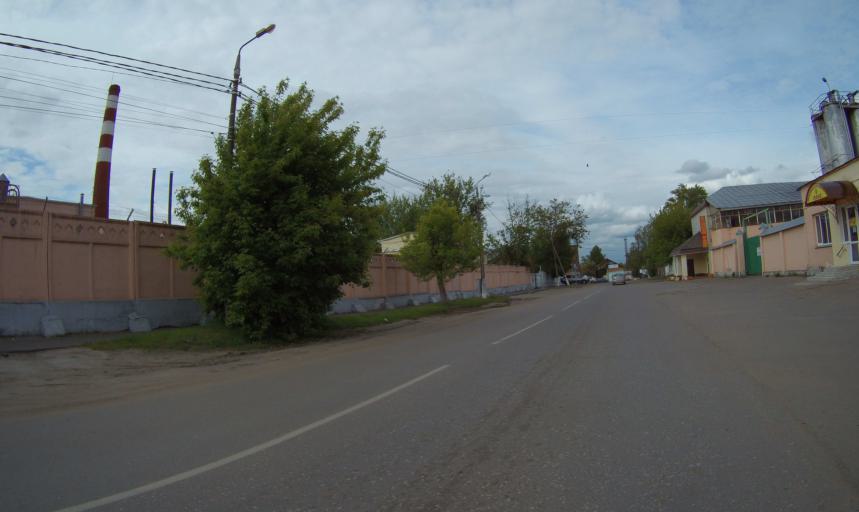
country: RU
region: Moskovskaya
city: Kolomna
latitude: 55.0926
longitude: 38.7798
